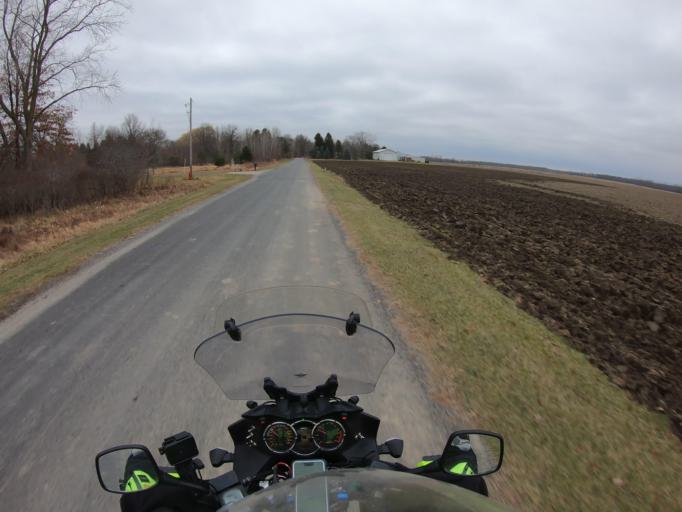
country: US
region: Michigan
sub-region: Saginaw County
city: Saint Charles
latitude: 43.3417
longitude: -84.1313
